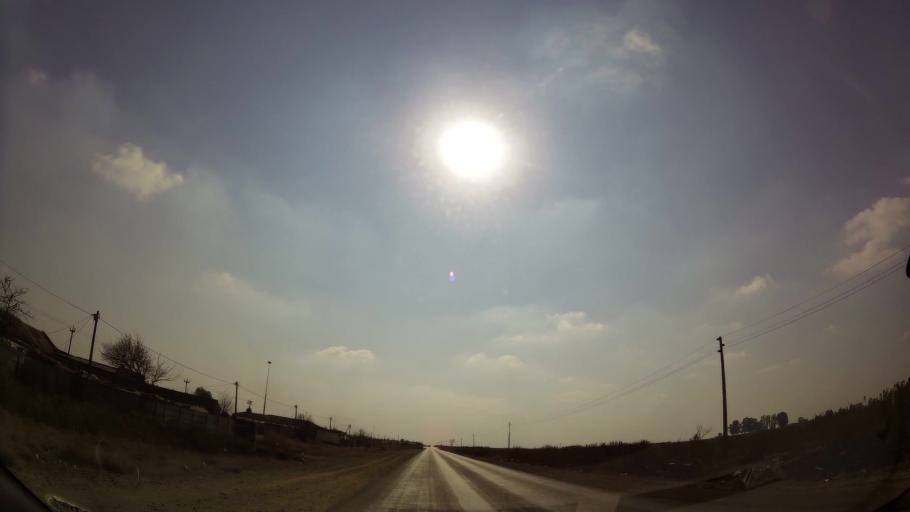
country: ZA
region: Gauteng
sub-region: Ekurhuleni Metropolitan Municipality
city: Springs
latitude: -26.1109
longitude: 28.4891
